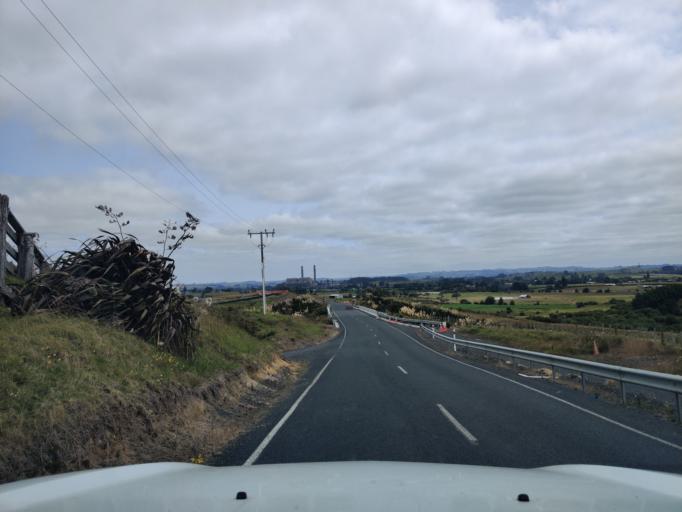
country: NZ
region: Waikato
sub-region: Waikato District
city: Te Kauwhata
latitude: -37.5225
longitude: 175.1762
